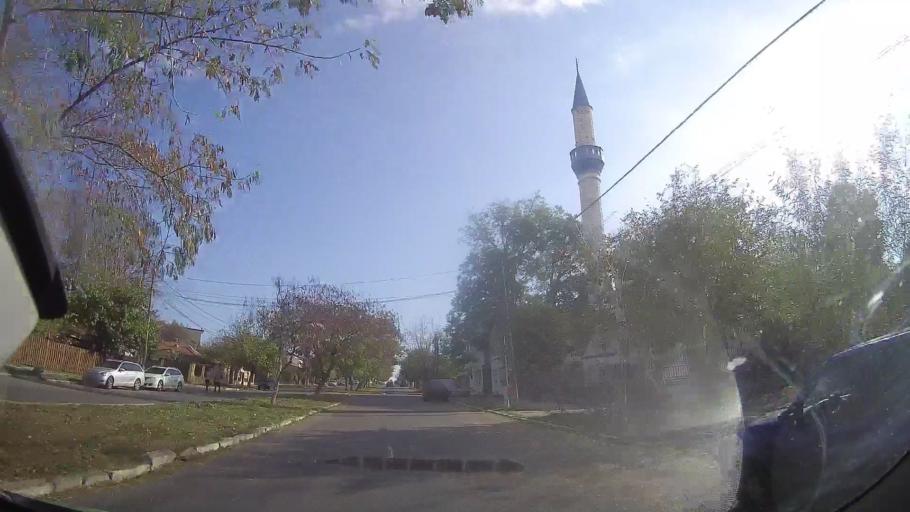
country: RO
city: Eforie Sud
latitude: 44.0217
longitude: 28.6464
